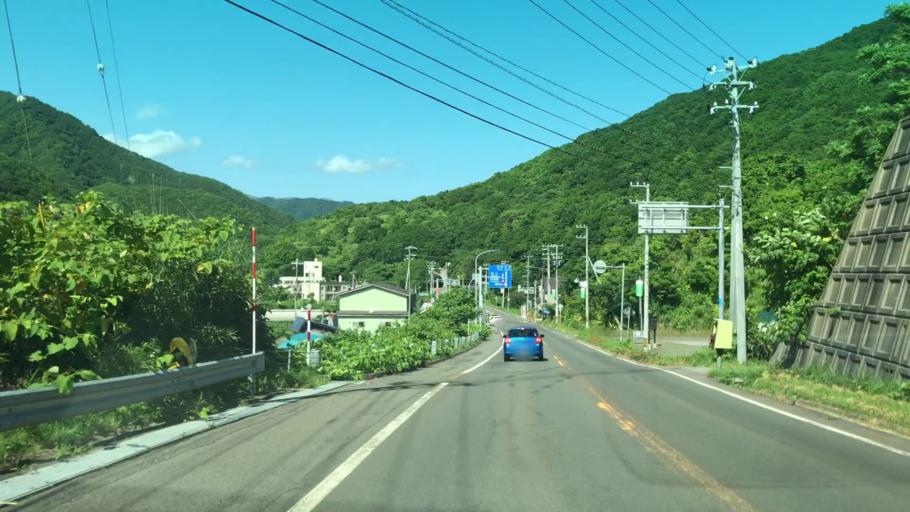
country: JP
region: Hokkaido
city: Iwanai
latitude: 43.1409
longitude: 140.4329
